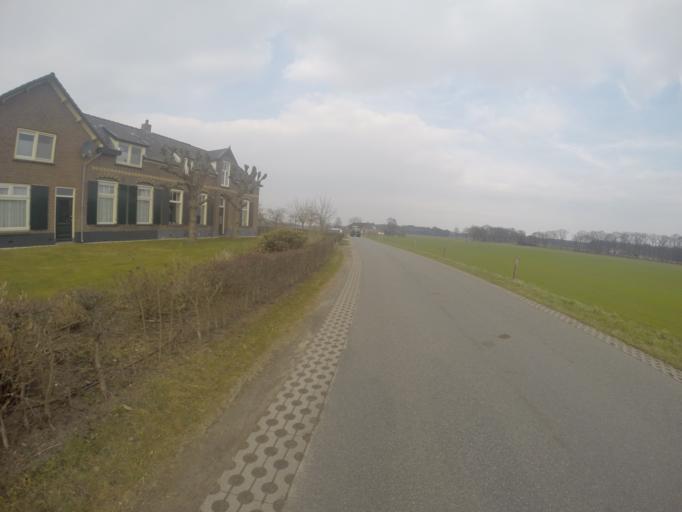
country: NL
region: Gelderland
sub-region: Gemeente Lochem
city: Almen
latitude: 52.1465
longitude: 6.2789
